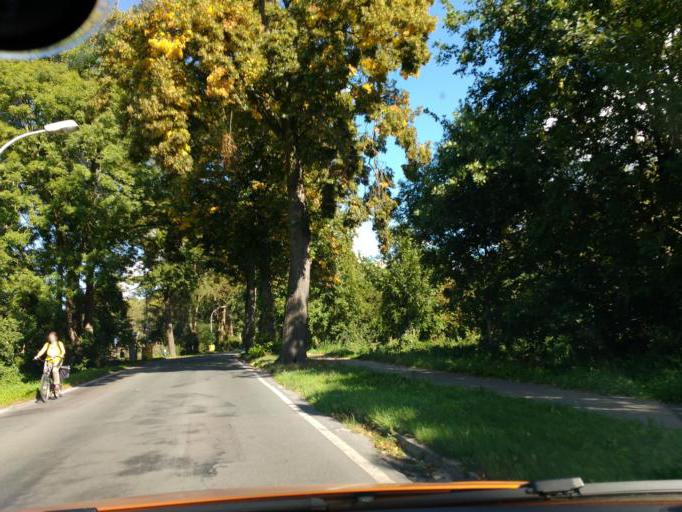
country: DE
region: Brandenburg
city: Bestensee
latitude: 52.2376
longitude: 13.6315
